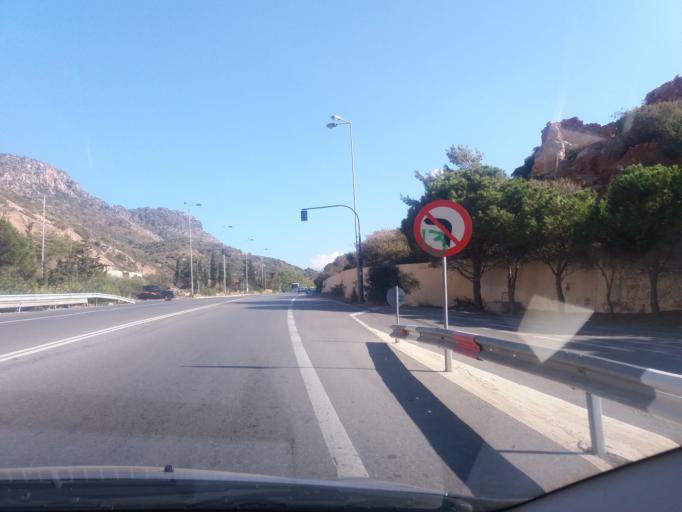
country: GR
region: Crete
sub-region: Nomos Lasithiou
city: Sision
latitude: 35.2847
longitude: 25.5432
